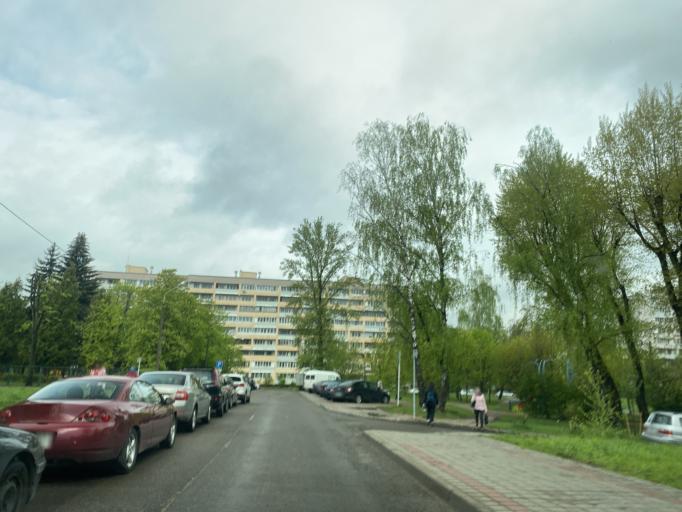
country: BY
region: Minsk
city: Minsk
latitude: 53.9231
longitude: 27.5854
